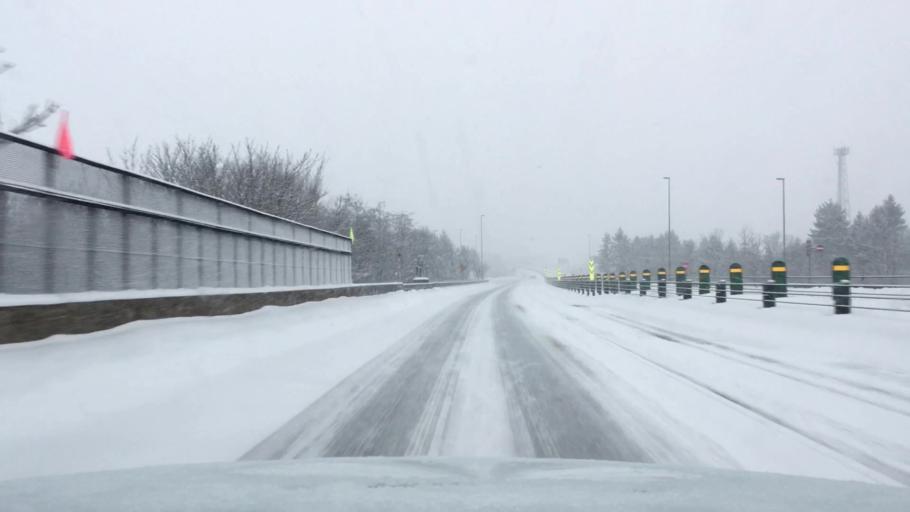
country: JP
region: Akita
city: Hanawa
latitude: 40.2552
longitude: 140.7662
